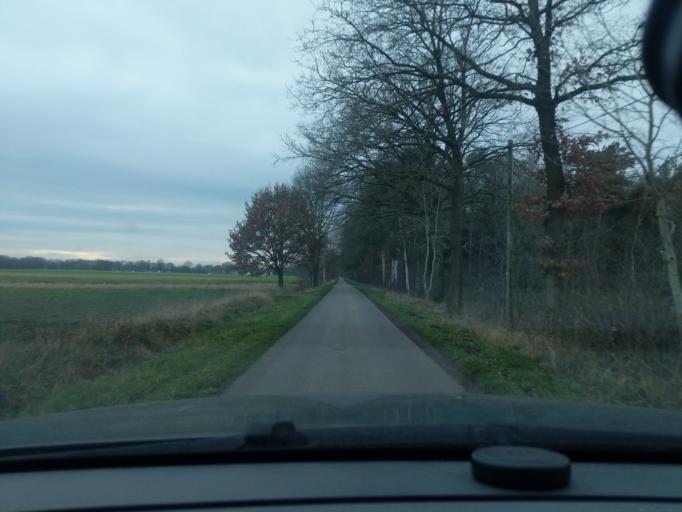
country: DE
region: Lower Saxony
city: Hemslingen
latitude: 53.0971
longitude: 9.6133
